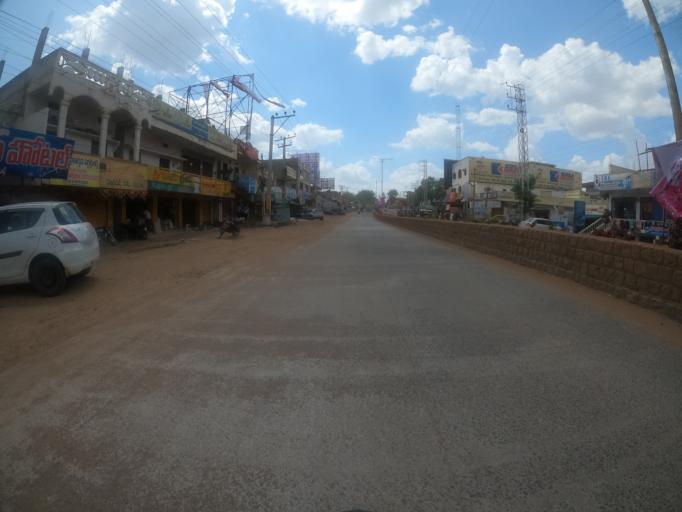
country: IN
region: Telangana
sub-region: Rangareddi
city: Sriramnagar
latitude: 17.3124
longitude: 78.1400
